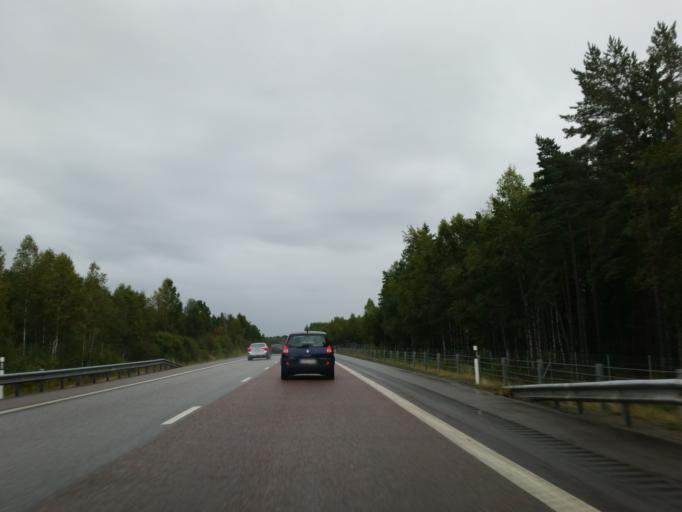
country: SE
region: Uppsala
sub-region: Enkopings Kommun
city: Dalby
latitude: 59.6105
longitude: 17.4151
